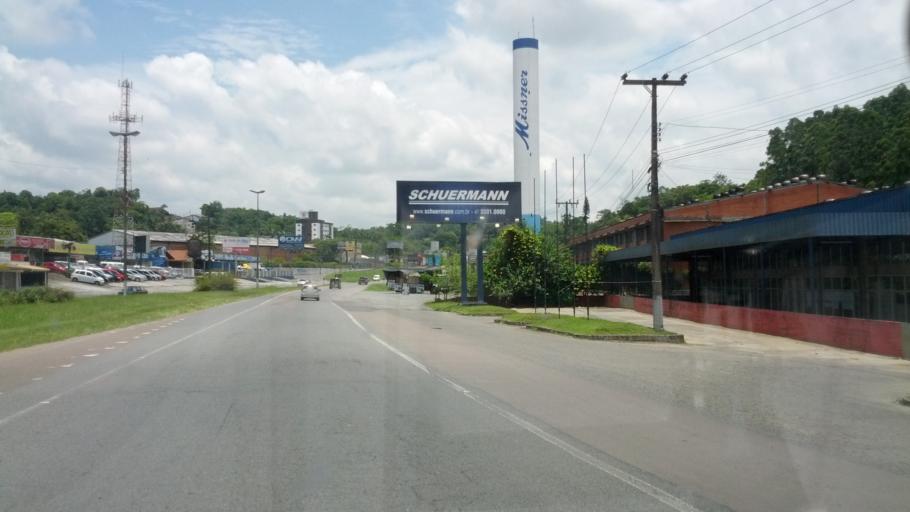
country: BR
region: Santa Catarina
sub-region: Blumenau
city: Blumenau
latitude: -26.8740
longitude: -49.1152
